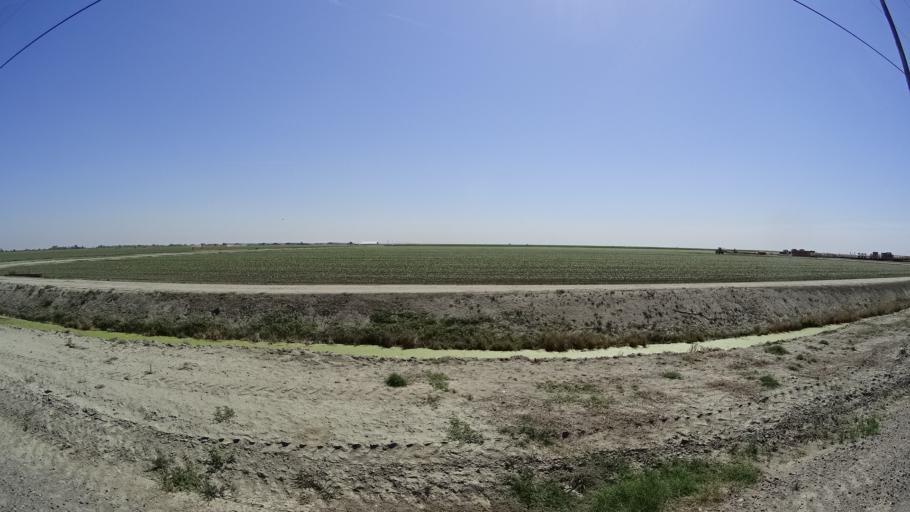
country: US
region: California
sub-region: Kings County
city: Corcoran
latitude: 36.0281
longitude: -119.5361
